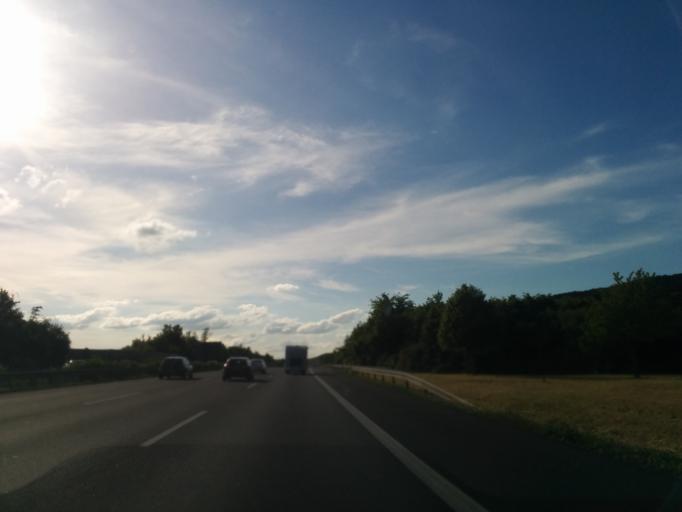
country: DE
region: Lower Saxony
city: Scheden
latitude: 51.3973
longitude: 9.7671
